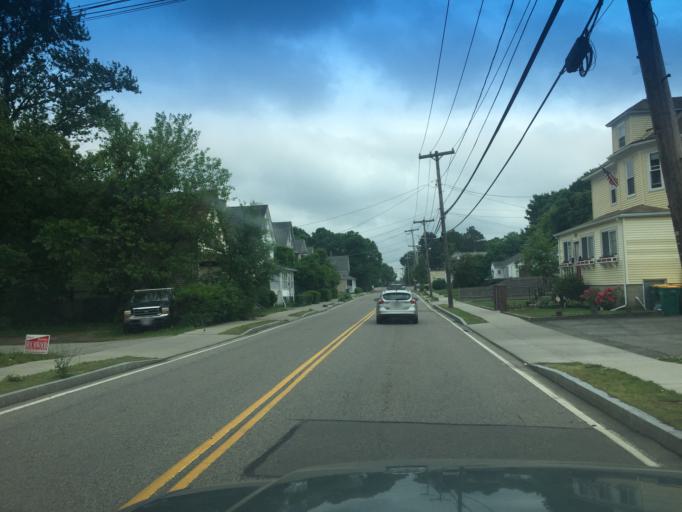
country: US
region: Massachusetts
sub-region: Norfolk County
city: Norwood
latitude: 42.2001
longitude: -71.2058
